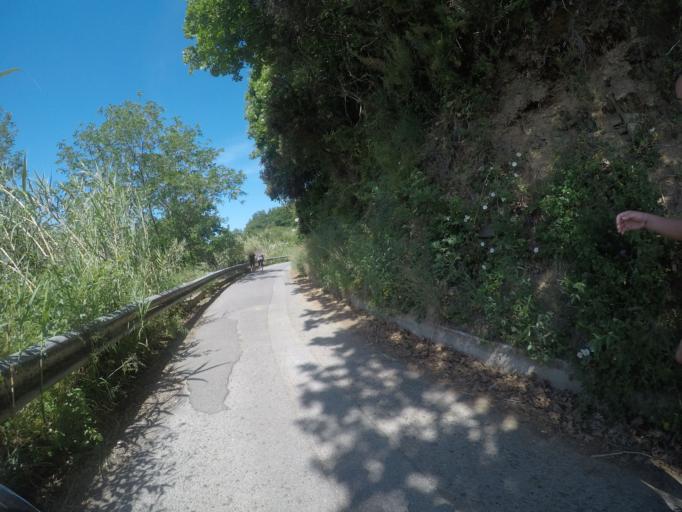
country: IT
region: Tuscany
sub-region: Provincia di Massa-Carrara
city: Massa
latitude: 44.0498
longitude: 10.1180
